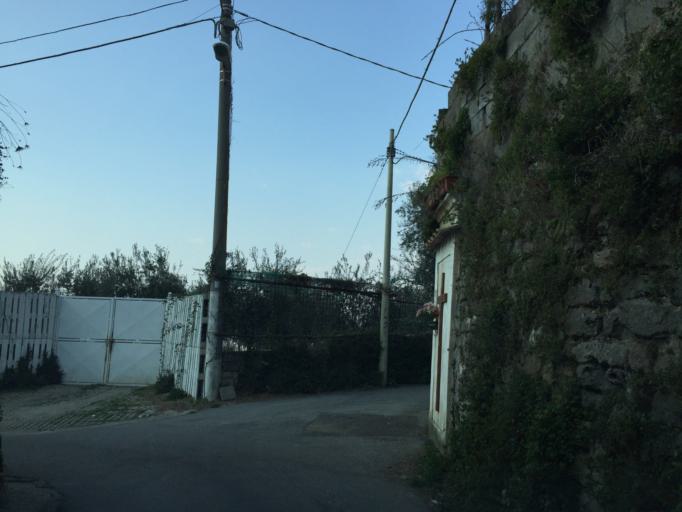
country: IT
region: Campania
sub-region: Provincia di Napoli
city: Piazza-Tralia-Pendolo
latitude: 40.6865
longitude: 14.4877
